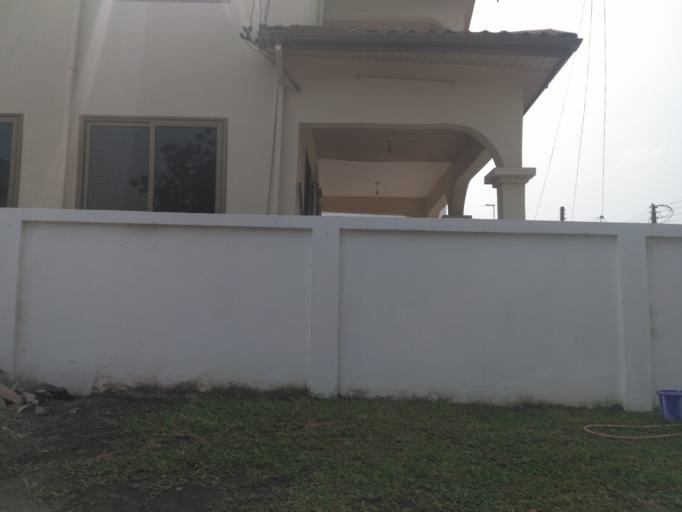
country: GH
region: Greater Accra
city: Accra
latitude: 5.5633
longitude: -0.1770
